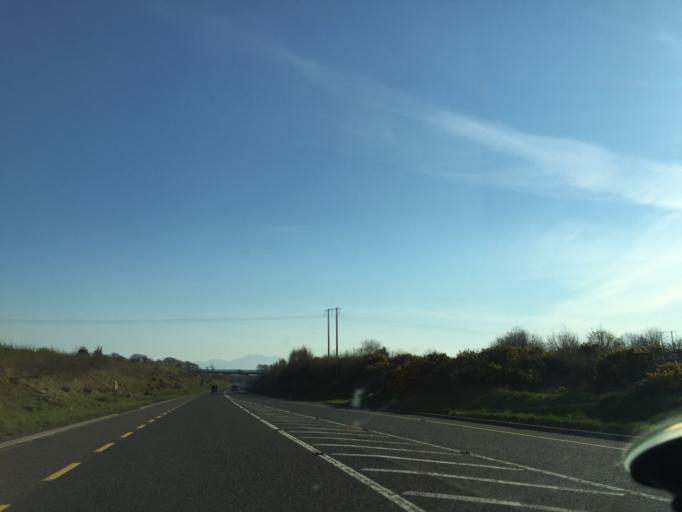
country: IE
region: Munster
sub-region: Ciarrai
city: Castleisland
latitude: 52.2075
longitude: -9.5672
